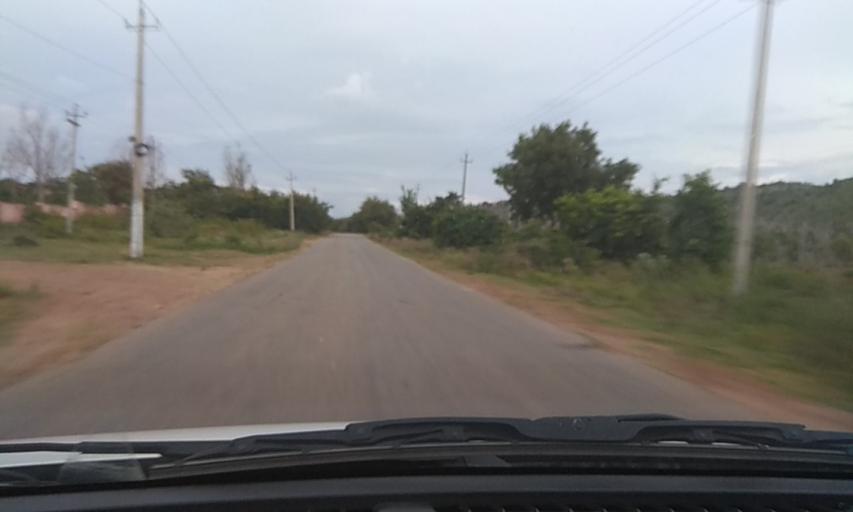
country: IN
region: Karnataka
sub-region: Chamrajnagar
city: Gundlupet
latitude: 11.7990
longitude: 76.7959
